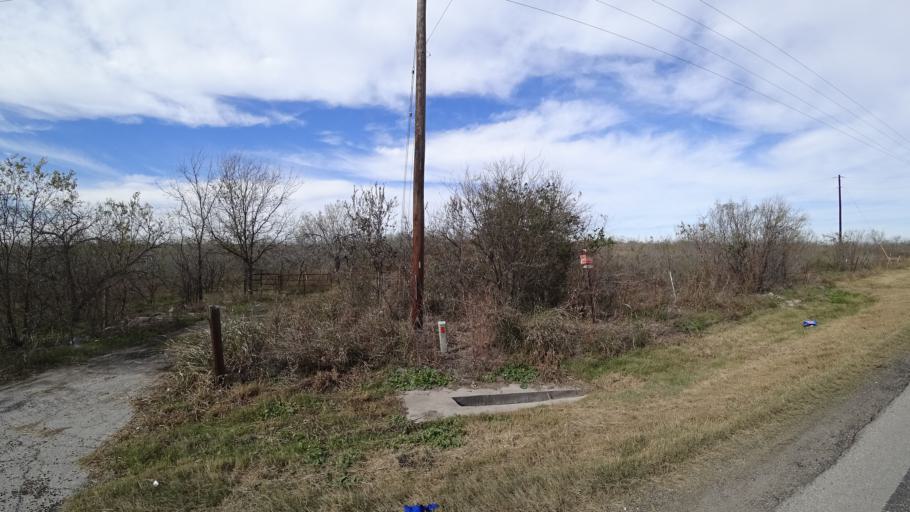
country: US
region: Texas
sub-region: Travis County
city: Onion Creek
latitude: 30.1211
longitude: -97.7151
